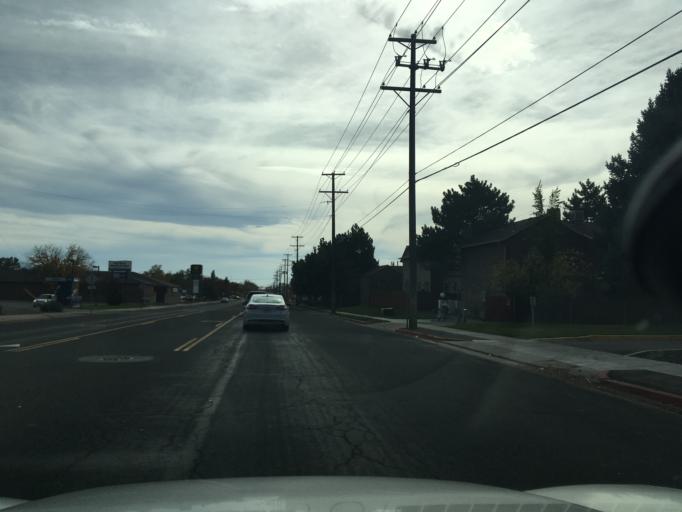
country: US
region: Utah
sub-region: Davis County
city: Layton
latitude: 41.0631
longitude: -111.9576
